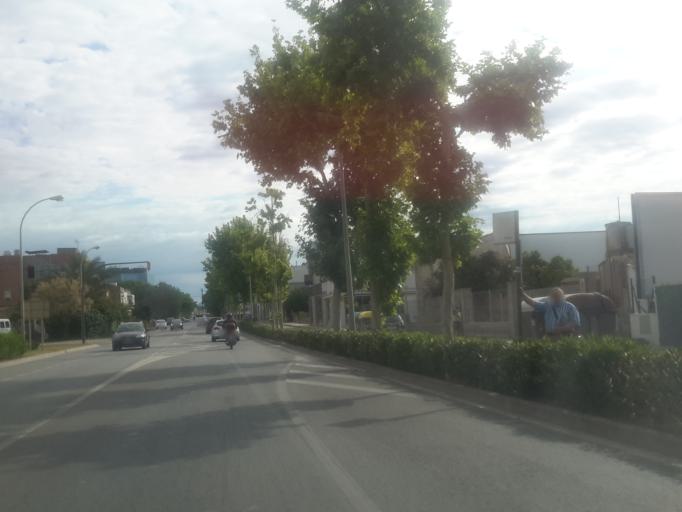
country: ES
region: Catalonia
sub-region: Provincia de Barcelona
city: Vilanova i la Geltru
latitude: 41.2258
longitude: 1.7337
